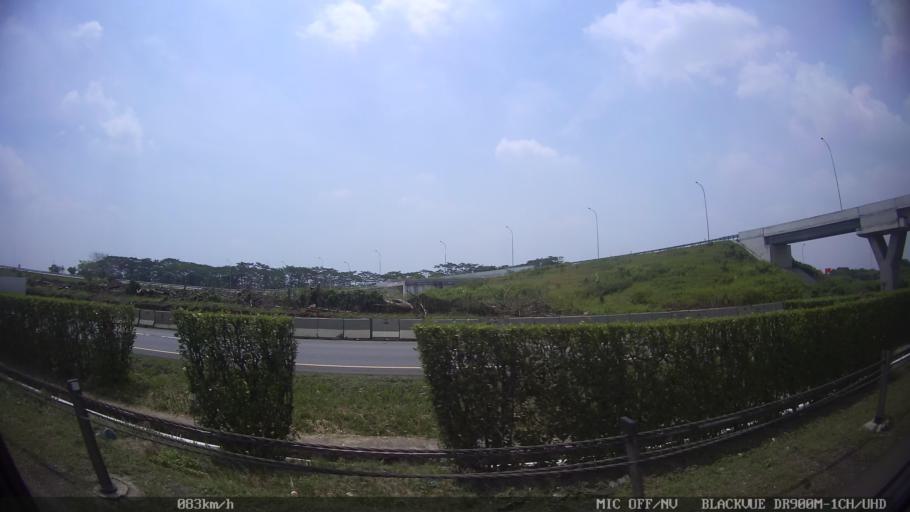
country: ID
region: Banten
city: Serang
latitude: -6.1388
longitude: 106.2478
